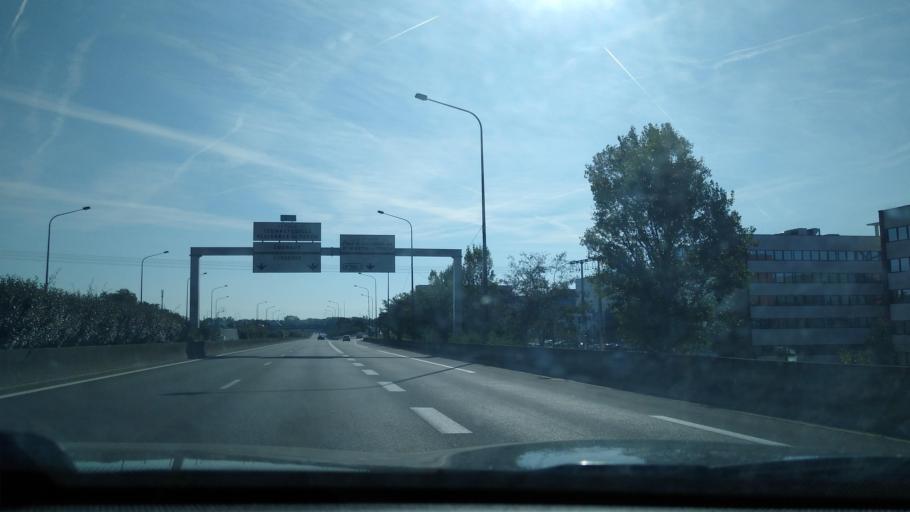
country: FR
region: Midi-Pyrenees
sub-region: Departement de la Haute-Garonne
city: Colomiers
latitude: 43.6005
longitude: 1.3652
